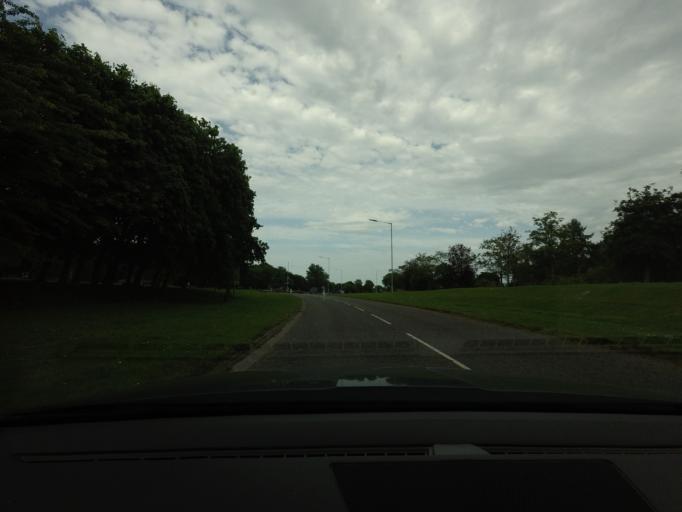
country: GB
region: Scotland
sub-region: Highland
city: Alness
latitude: 57.6919
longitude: -4.2718
